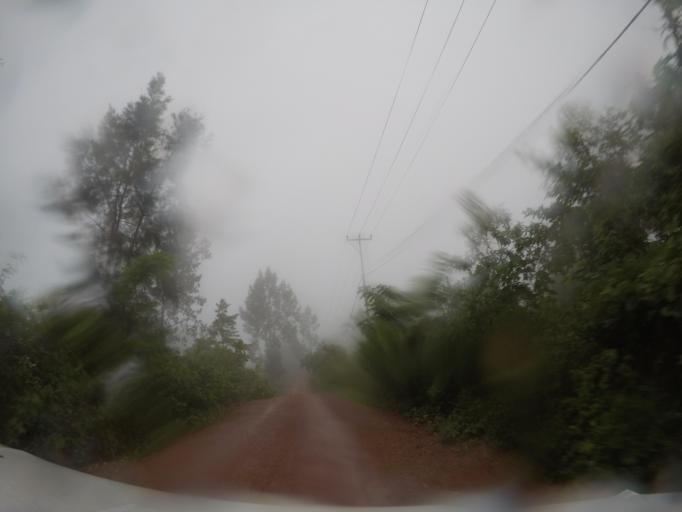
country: TL
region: Baucau
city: Venilale
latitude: -8.6354
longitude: 126.4208
